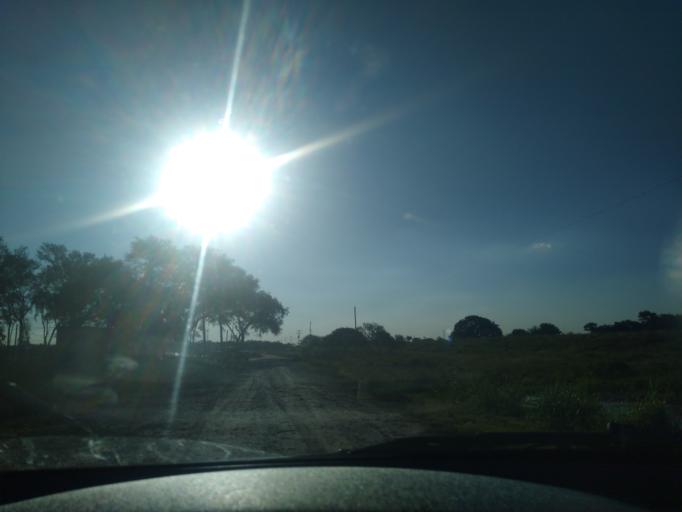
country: AR
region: Chaco
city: Resistencia
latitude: -27.4090
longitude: -58.9513
